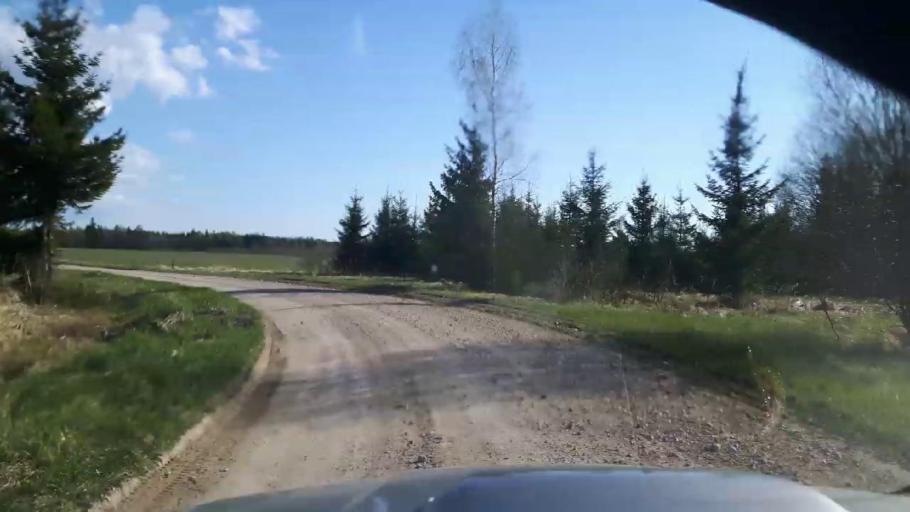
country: EE
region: Paernumaa
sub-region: Tootsi vald
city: Tootsi
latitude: 58.4397
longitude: 24.8551
